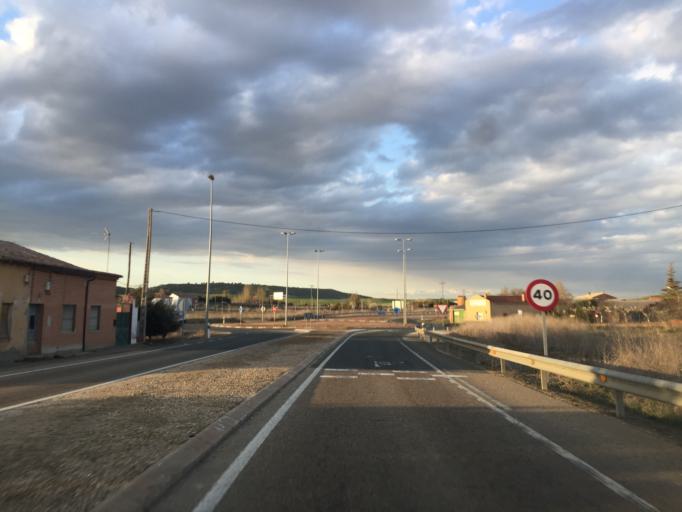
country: ES
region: Castille and Leon
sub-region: Provincia de Palencia
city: Soto de Cerrato
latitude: 41.9809
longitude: -4.4316
